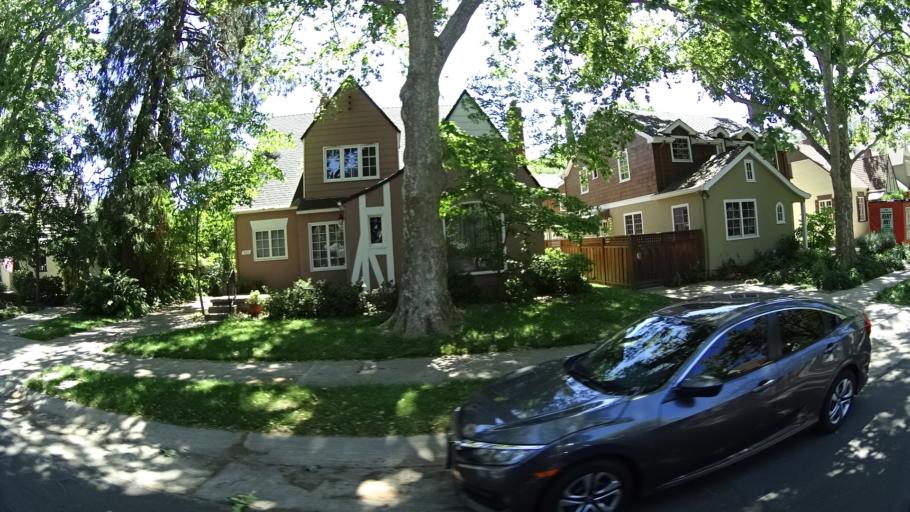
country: US
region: California
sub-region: Sacramento County
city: Sacramento
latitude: 38.5758
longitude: -121.4545
